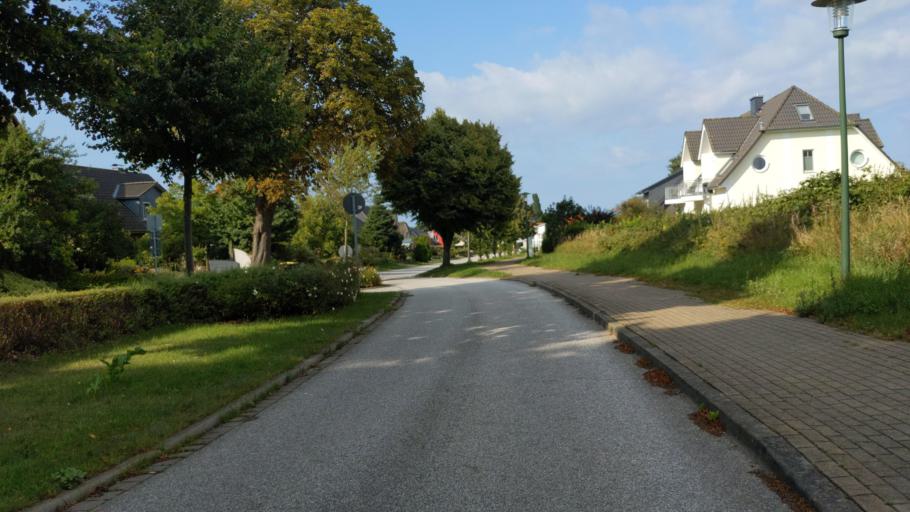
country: DE
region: Mecklenburg-Vorpommern
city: Kalkhorst
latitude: 53.9822
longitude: 11.0070
